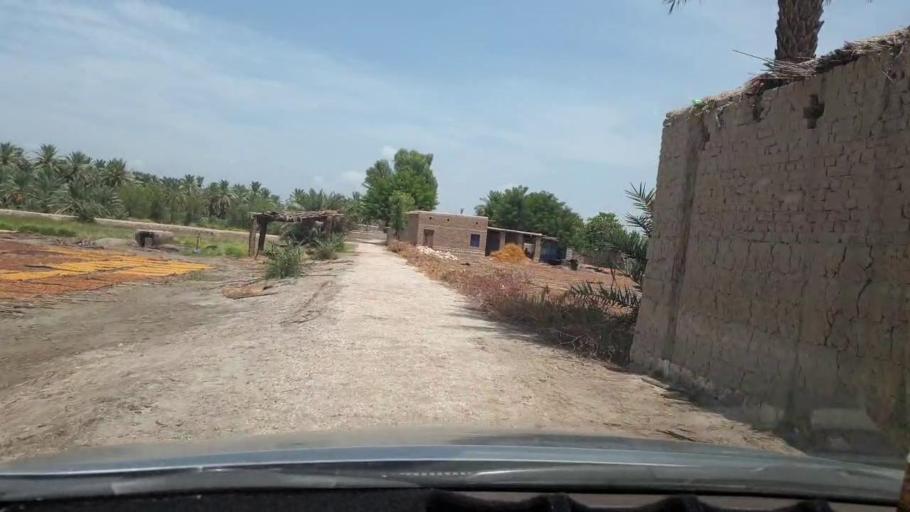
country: PK
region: Sindh
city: Khairpur
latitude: 27.4447
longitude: 68.7767
